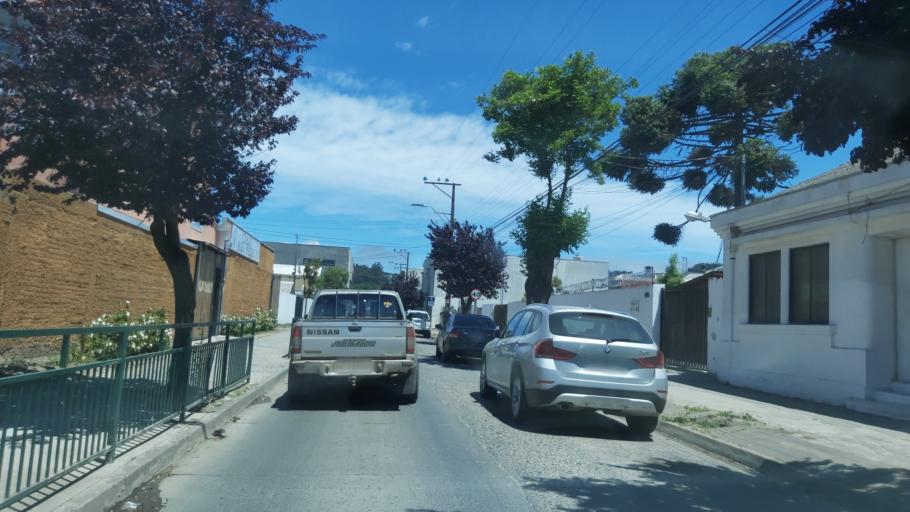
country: CL
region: Maule
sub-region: Provincia de Talca
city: Constitucion
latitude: -35.3291
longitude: -72.4100
